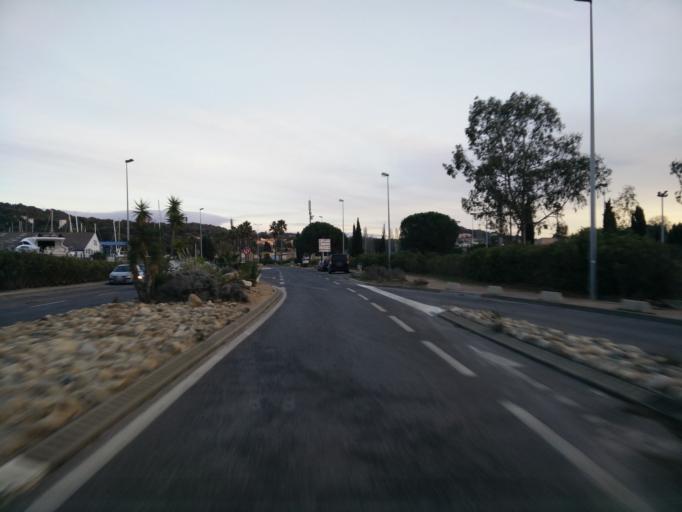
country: FR
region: Provence-Alpes-Cote d'Azur
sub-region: Departement du Var
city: Saint-Mandrier-sur-Mer
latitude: 43.0788
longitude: 5.9044
